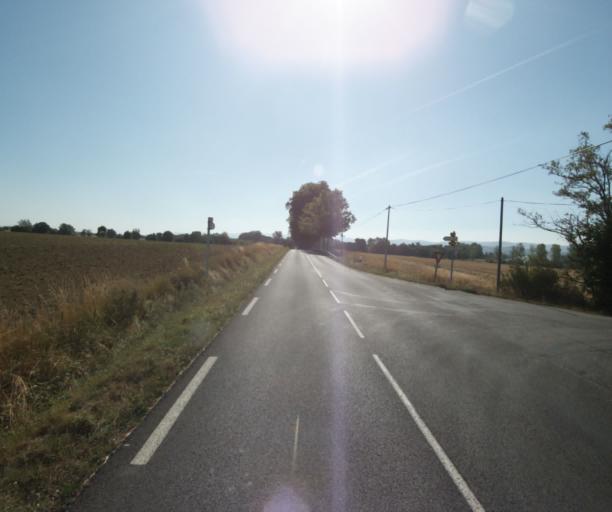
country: FR
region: Midi-Pyrenees
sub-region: Departement de la Haute-Garonne
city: Revel
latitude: 43.4699
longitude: 1.9611
